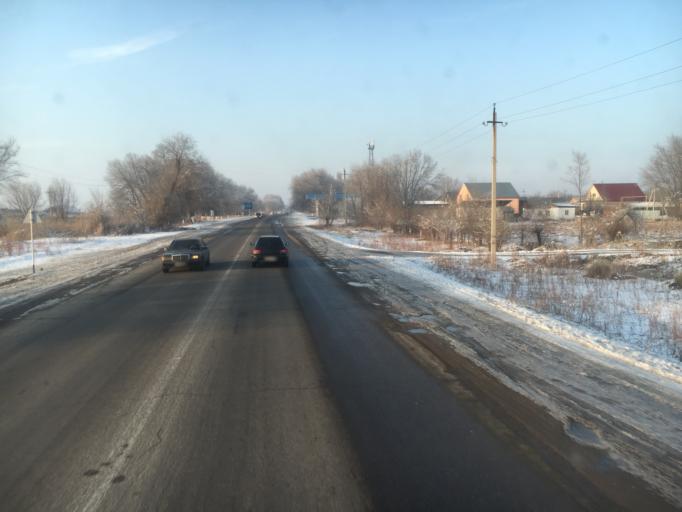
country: KZ
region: Almaty Oblysy
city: Burunday
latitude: 43.3339
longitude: 76.6610
